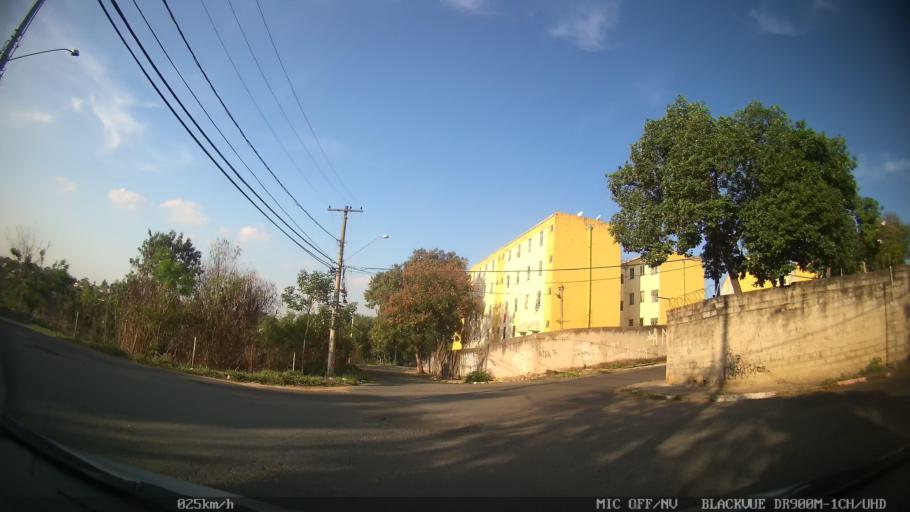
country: BR
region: Sao Paulo
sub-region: Campinas
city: Campinas
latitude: -22.9738
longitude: -47.1195
